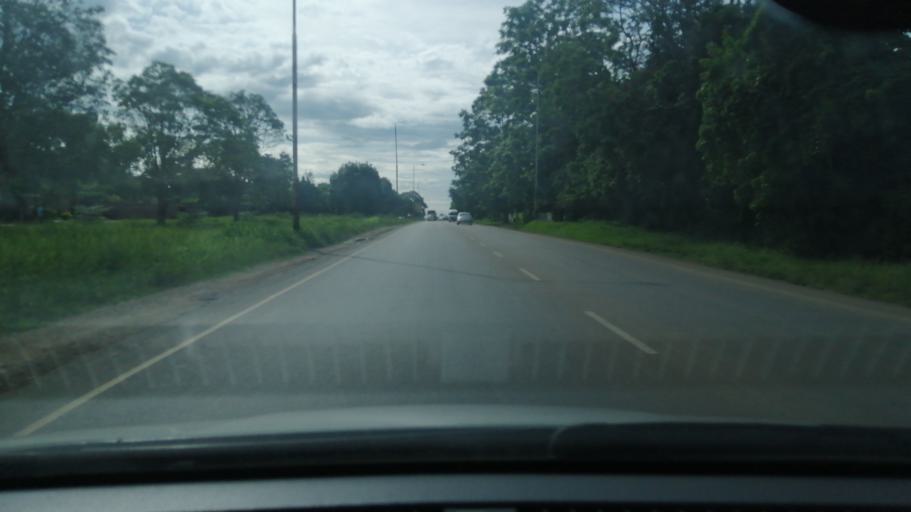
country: ZW
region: Harare
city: Harare
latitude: -17.7630
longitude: 30.9858
